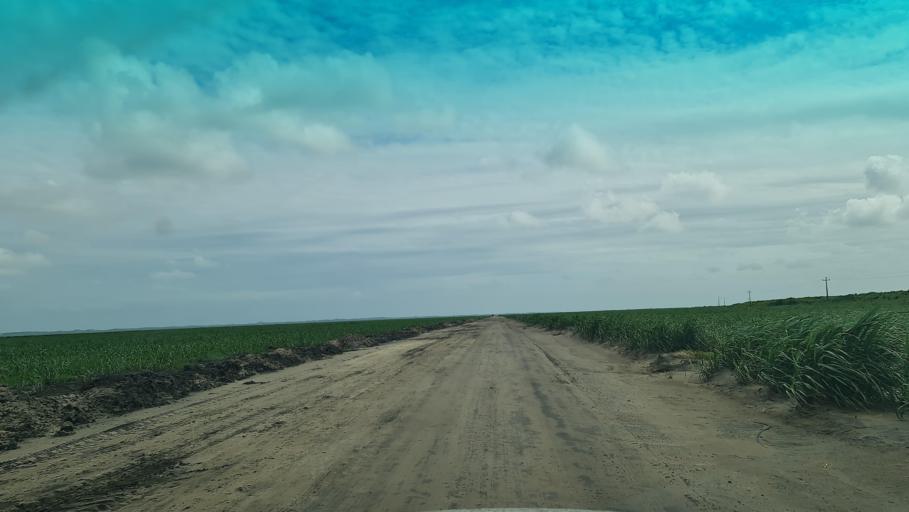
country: MZ
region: Maputo
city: Manhica
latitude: -25.4670
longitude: 32.8177
